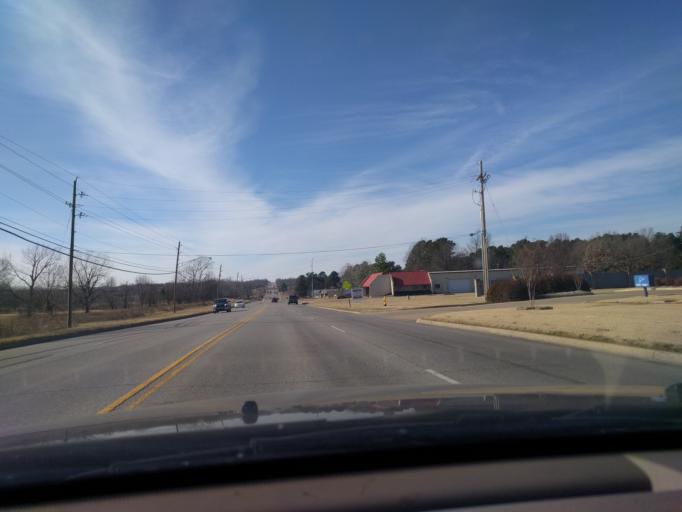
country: US
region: Oklahoma
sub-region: Tulsa County
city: Broken Arrow
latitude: 36.0609
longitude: -95.7285
